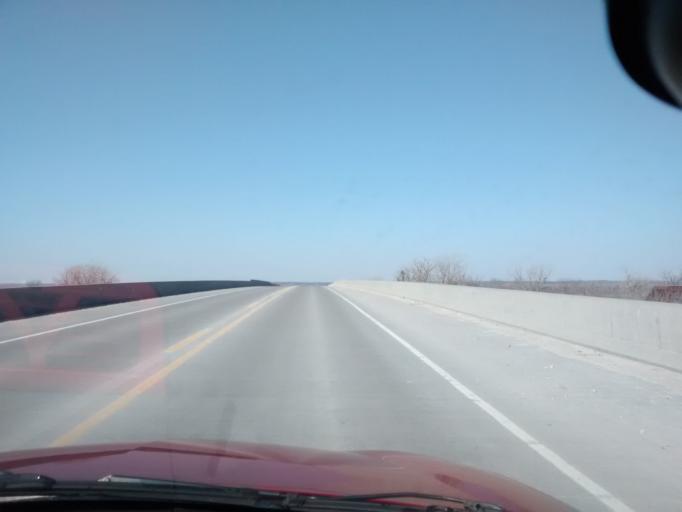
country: US
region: Iowa
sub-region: Pottawattamie County
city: Carter Lake
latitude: 41.3606
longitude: -95.8778
